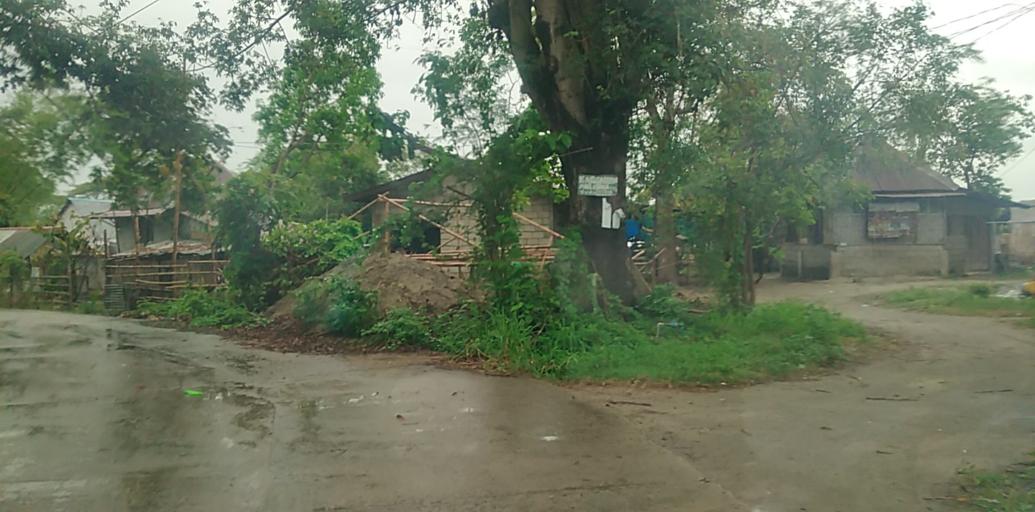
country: PH
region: Central Luzon
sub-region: Province of Pampanga
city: San Antonio
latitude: 15.1528
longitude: 120.6853
